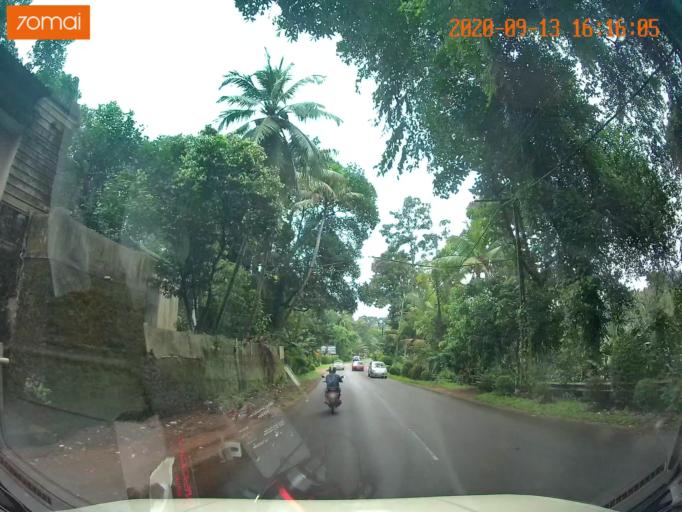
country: IN
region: Kerala
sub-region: Kottayam
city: Palackattumala
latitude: 9.6951
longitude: 76.6461
